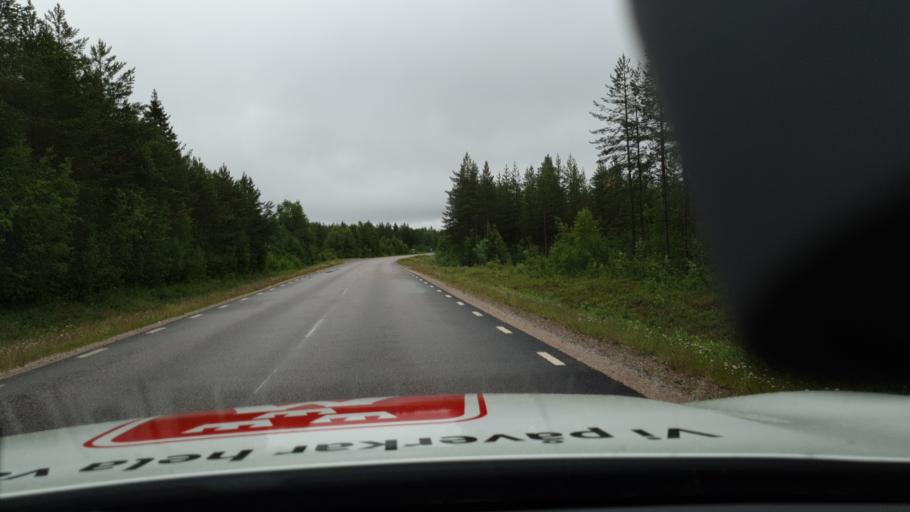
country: SE
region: Norrbotten
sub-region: Overtornea Kommun
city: OEvertornea
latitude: 66.3973
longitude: 23.5543
